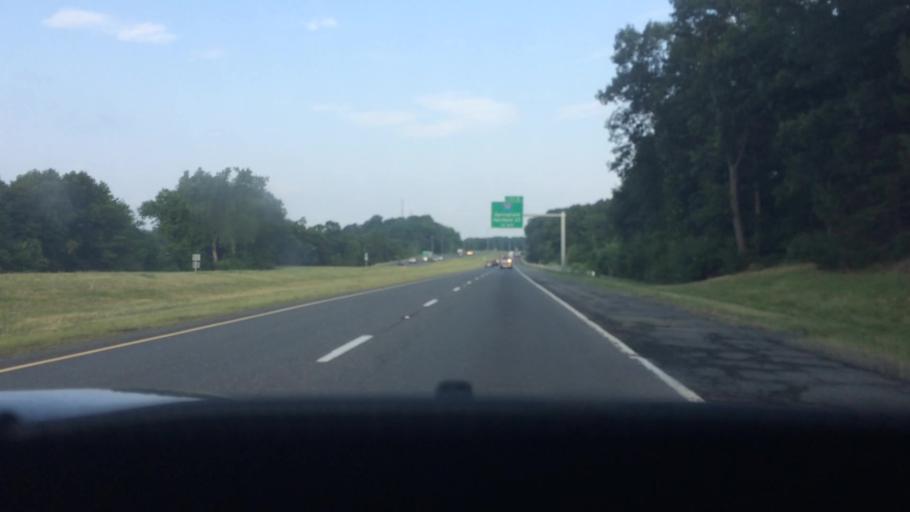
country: US
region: Massachusetts
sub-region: Hampden County
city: Ludlow
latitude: 42.1623
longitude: -72.5298
